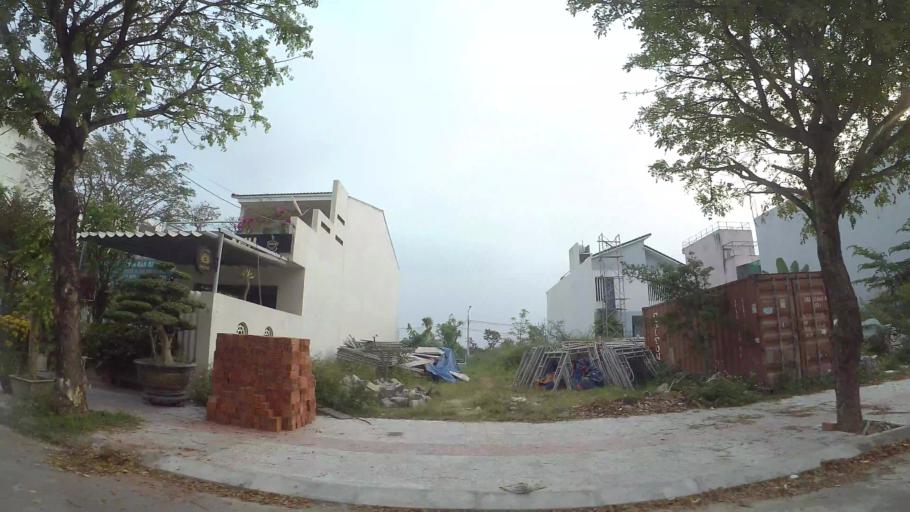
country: VN
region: Da Nang
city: Cam Le
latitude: 16.0221
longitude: 108.2284
